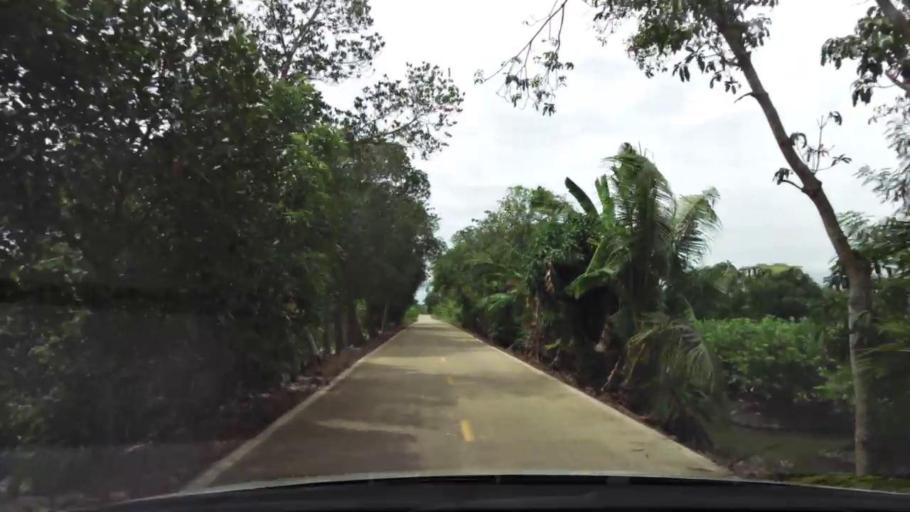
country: TH
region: Ratchaburi
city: Damnoen Saduak
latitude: 13.5478
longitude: 99.9840
